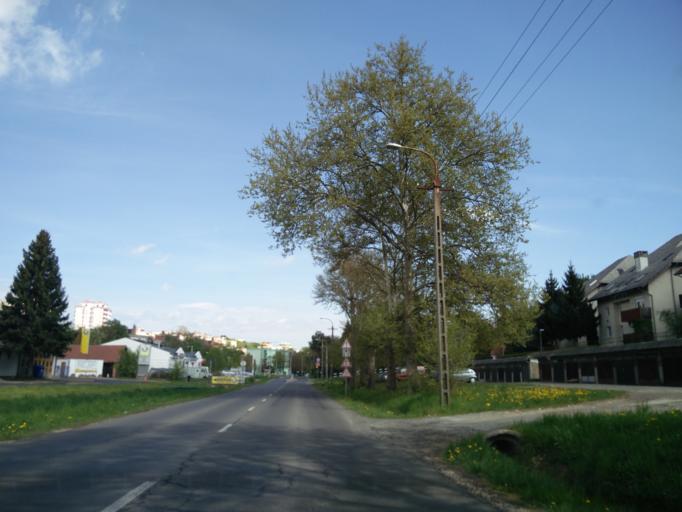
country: HU
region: Zala
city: Zalaegerszeg
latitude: 46.8303
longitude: 16.8279
